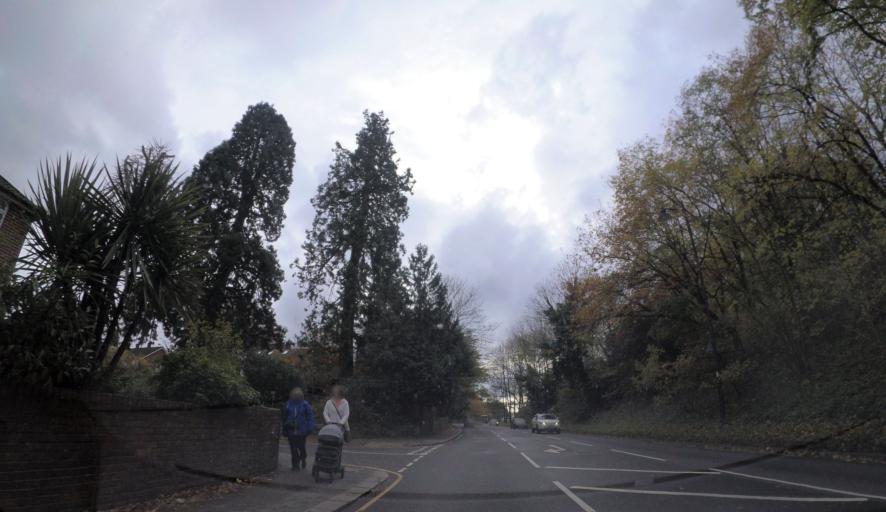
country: GB
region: England
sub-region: Surrey
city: Reigate
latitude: 51.2334
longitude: -0.2034
